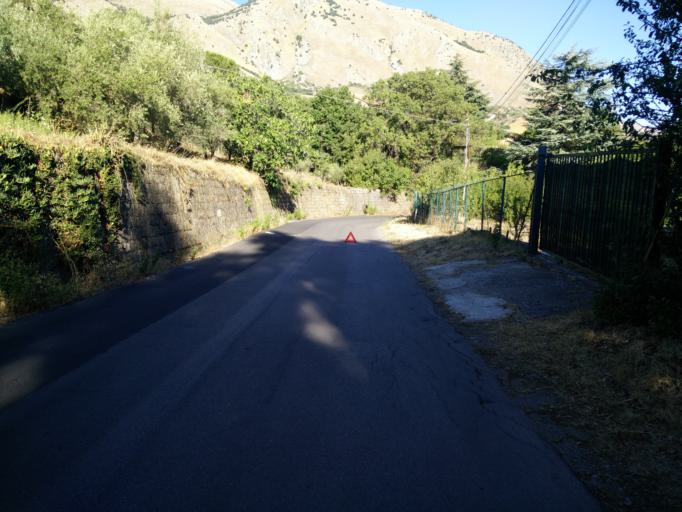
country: IT
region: Sicily
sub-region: Palermo
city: Castelbuono
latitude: 37.9224
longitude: 14.0863
